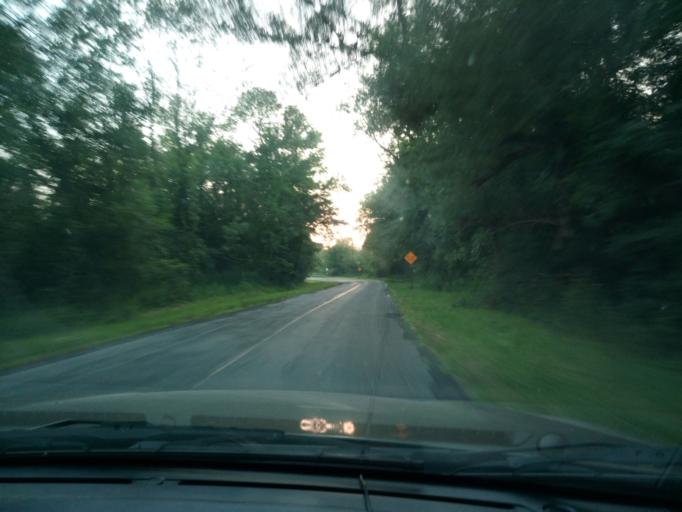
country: US
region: New York
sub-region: Wayne County
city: Clyde
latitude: 43.0210
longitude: -76.8033
